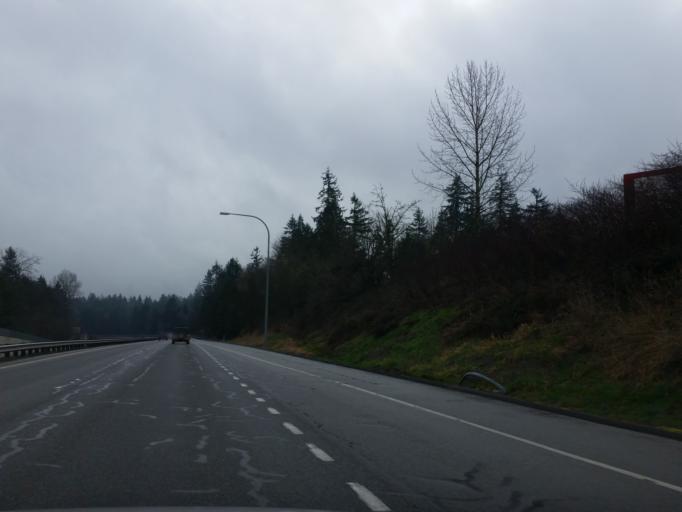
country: US
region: Washington
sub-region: Snohomish County
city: Maltby
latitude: 47.7950
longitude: -122.1252
